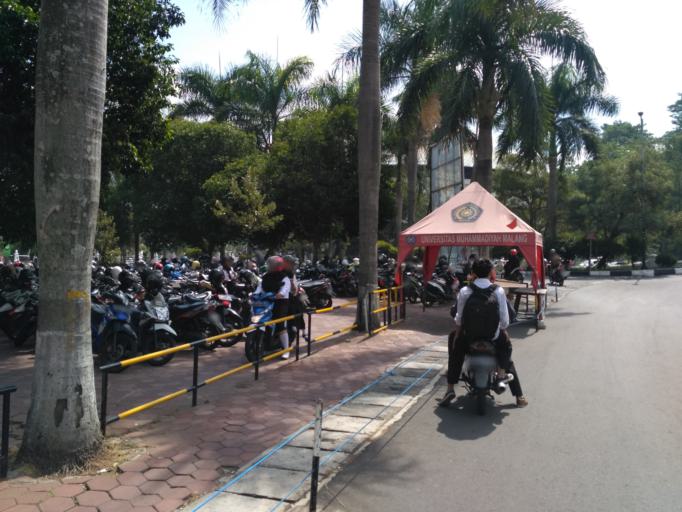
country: ID
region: East Java
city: Malang
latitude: -7.9209
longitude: 112.5962
